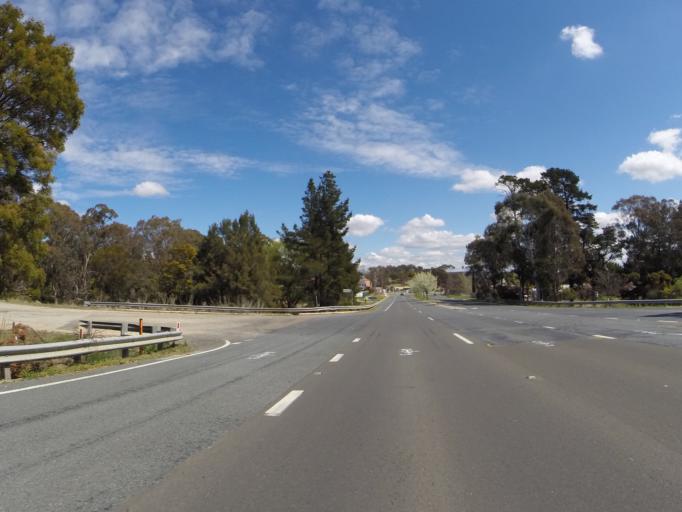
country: AU
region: New South Wales
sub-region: Goulburn Mulwaree
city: Goulburn
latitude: -34.7466
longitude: 149.7538
